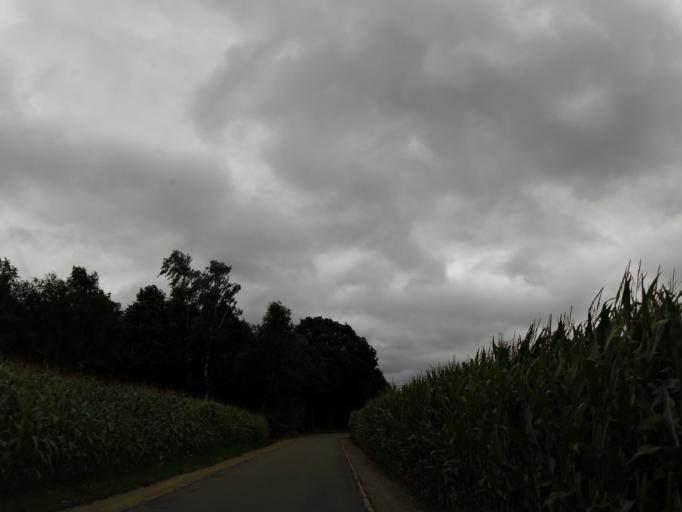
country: BE
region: Flanders
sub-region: Provincie Limburg
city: Bree
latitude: 51.1190
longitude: 5.6235
